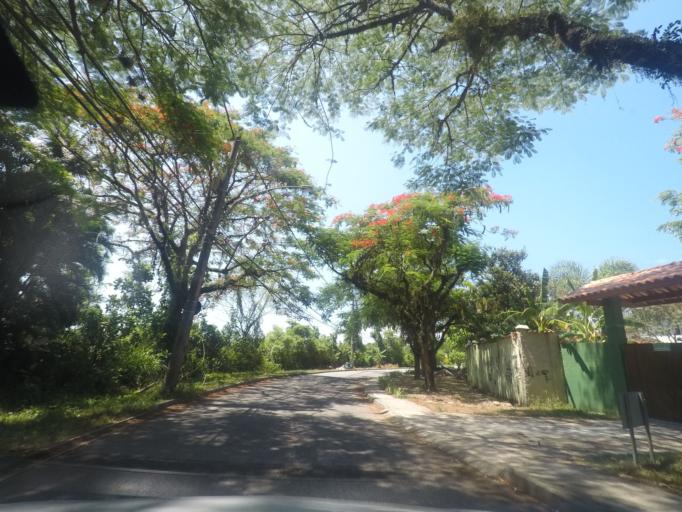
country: BR
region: Rio de Janeiro
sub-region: Nilopolis
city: Nilopolis
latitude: -22.9835
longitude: -43.4590
